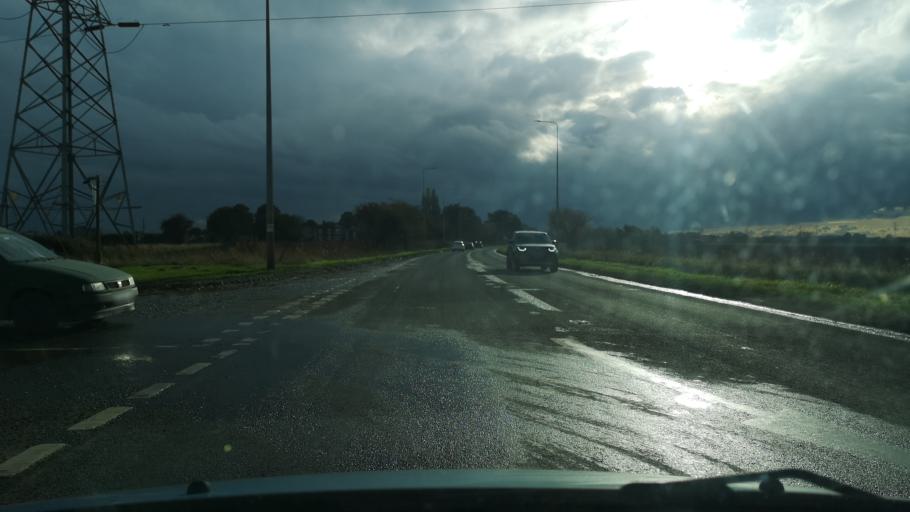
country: GB
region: England
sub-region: North Lincolnshire
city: Gunness
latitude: 53.5826
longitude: -0.7379
